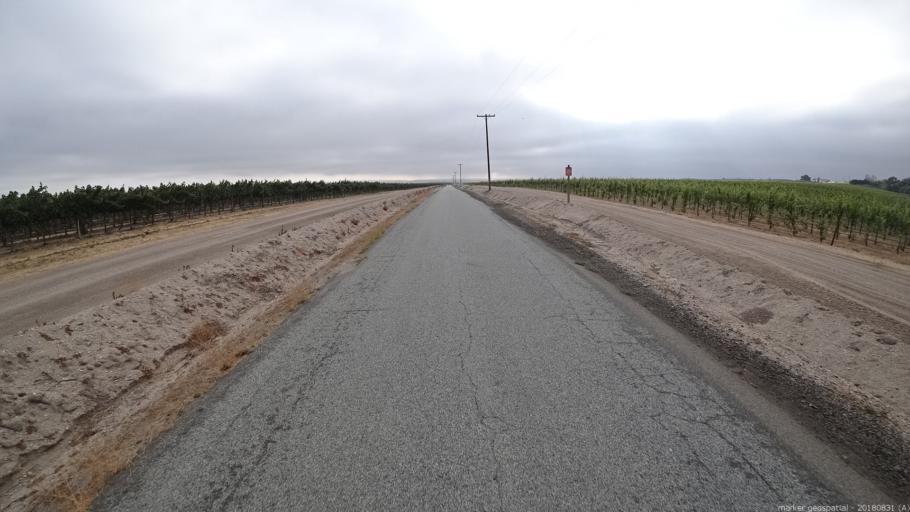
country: US
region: California
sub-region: Monterey County
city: King City
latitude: 36.1398
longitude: -121.0983
